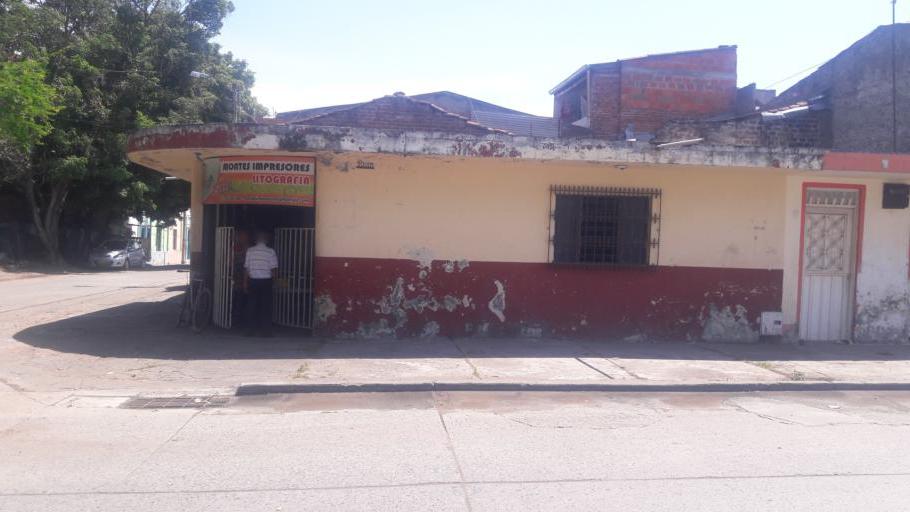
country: CO
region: Valle del Cauca
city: Tulua
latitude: 4.0905
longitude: -76.1977
